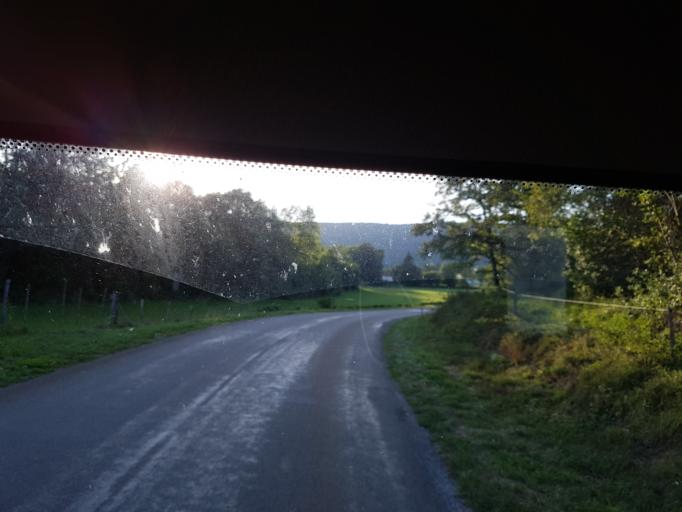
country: FR
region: Franche-Comte
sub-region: Departement du Jura
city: Moirans-en-Montagne
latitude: 46.4000
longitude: 5.6569
